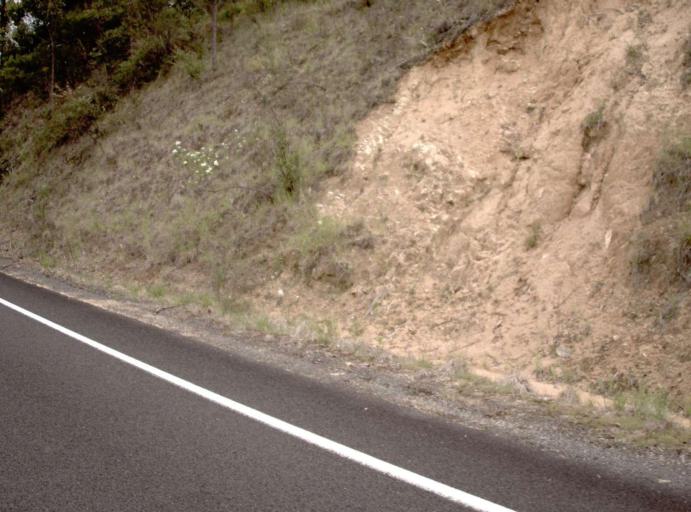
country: AU
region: New South Wales
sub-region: Bombala
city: Bombala
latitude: -37.2490
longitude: 149.2533
